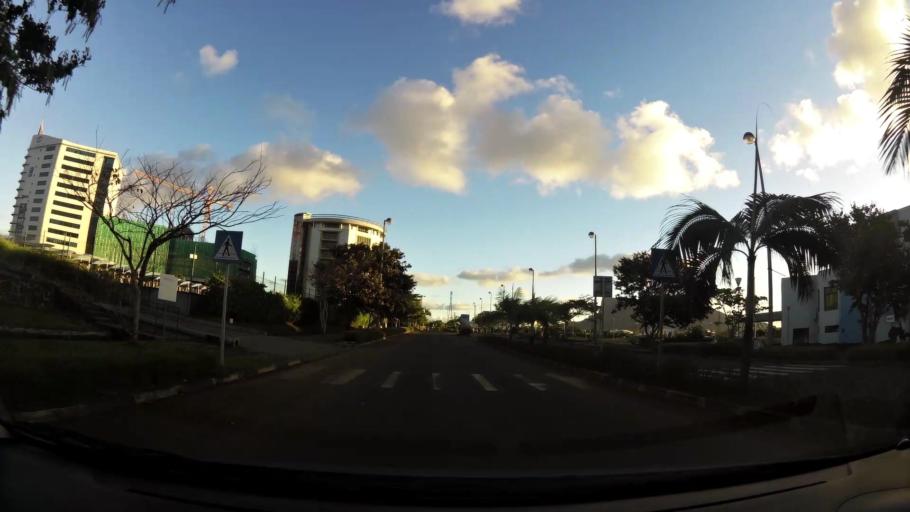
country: MU
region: Plaines Wilhems
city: Ebene
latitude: -20.2462
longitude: 57.4926
